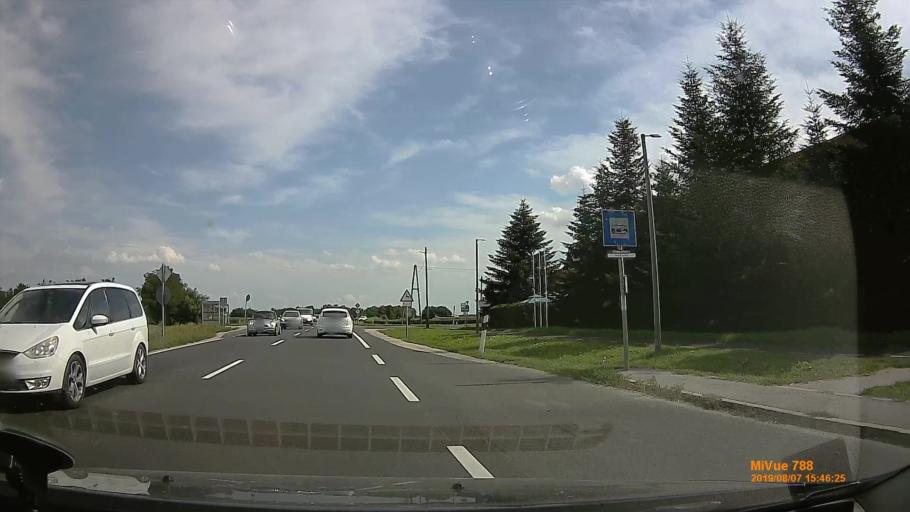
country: HU
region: Vas
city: Szombathely
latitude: 47.1853
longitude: 16.6210
